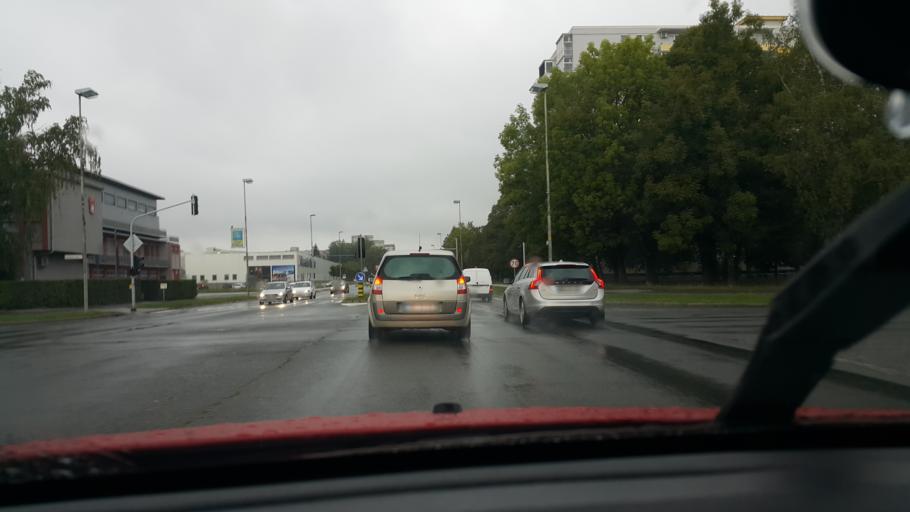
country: SI
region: Maribor
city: Maribor
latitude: 46.5401
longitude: 15.6450
